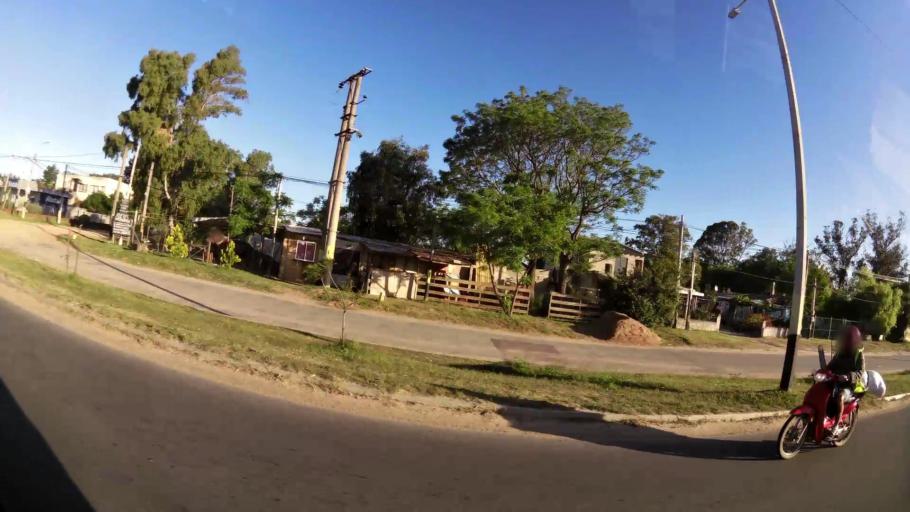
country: UY
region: Canelones
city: Paso de Carrasco
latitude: -34.8548
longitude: -56.0425
